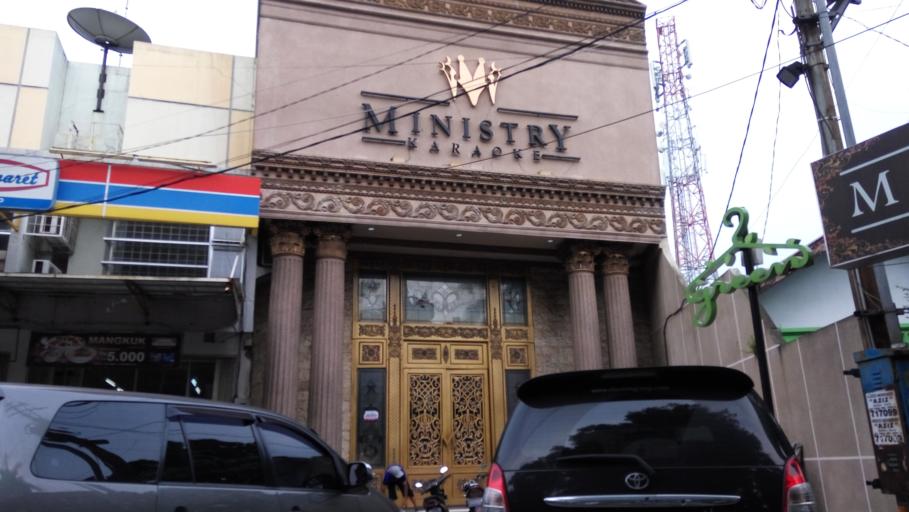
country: ID
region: East Java
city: Malang
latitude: -7.9796
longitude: 112.6142
